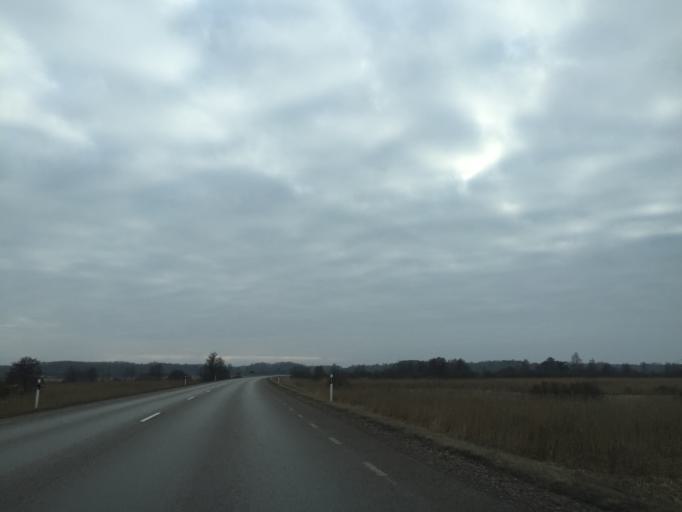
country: EE
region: Saare
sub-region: Orissaare vald
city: Orissaare
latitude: 58.5396
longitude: 23.1195
